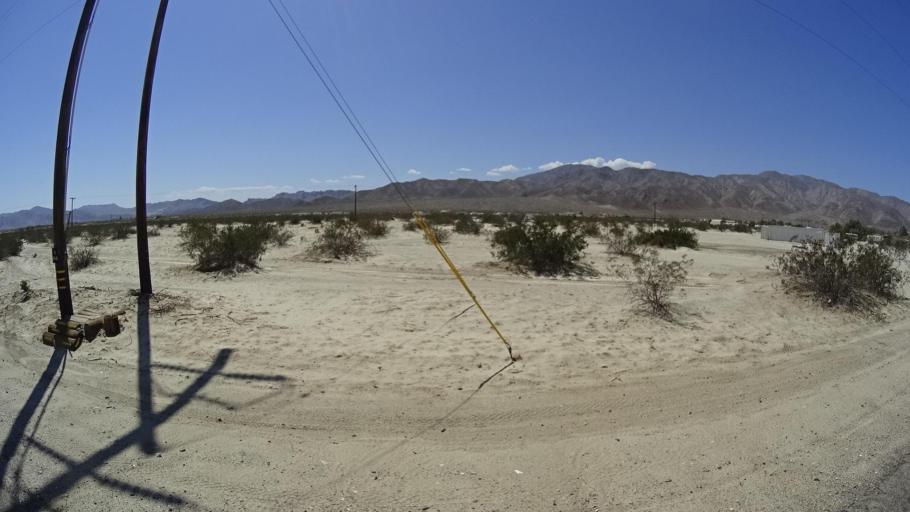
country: US
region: California
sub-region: Imperial County
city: Salton City
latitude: 33.1011
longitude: -116.1168
